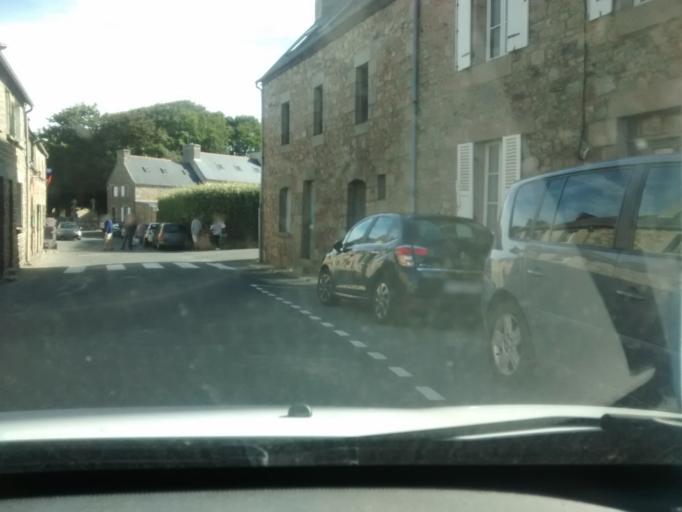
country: FR
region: Brittany
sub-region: Departement des Cotes-d'Armor
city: Plougrescant
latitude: 48.8403
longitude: -3.2290
